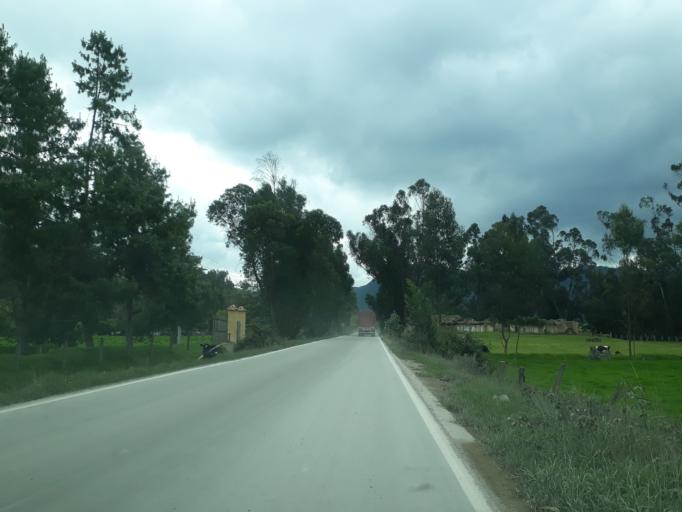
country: CO
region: Cundinamarca
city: Ubate
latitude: 5.3241
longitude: -73.7671
